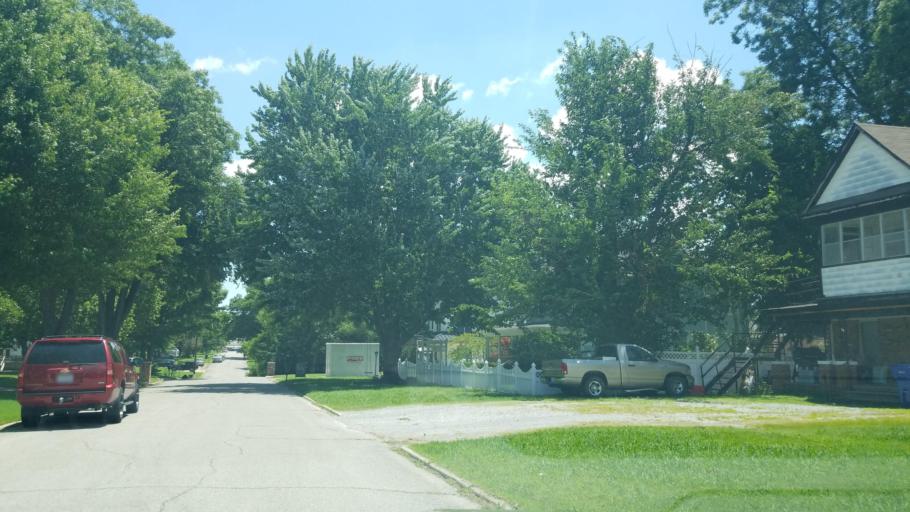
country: US
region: Oklahoma
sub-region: Tulsa County
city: Broken Arrow
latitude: 36.0514
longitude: -95.7878
